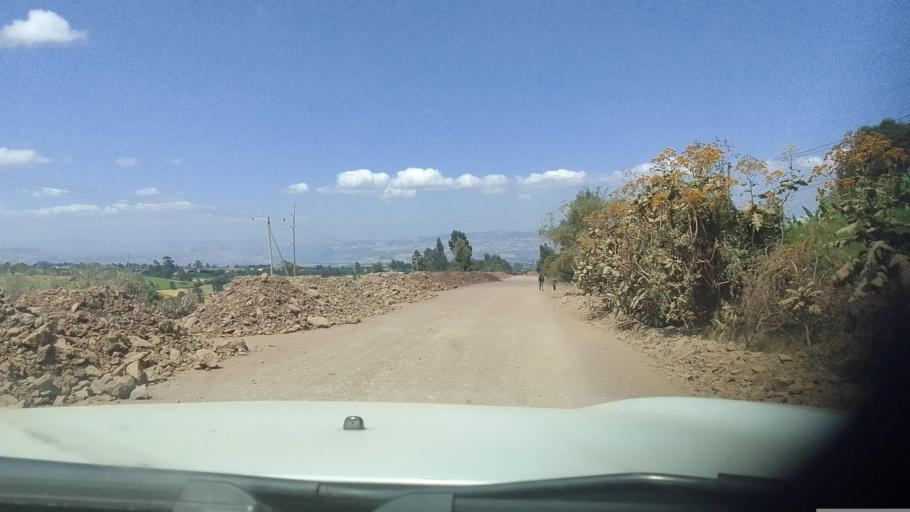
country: ET
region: Oromiya
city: Hagere Hiywet
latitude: 8.8566
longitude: 37.8922
